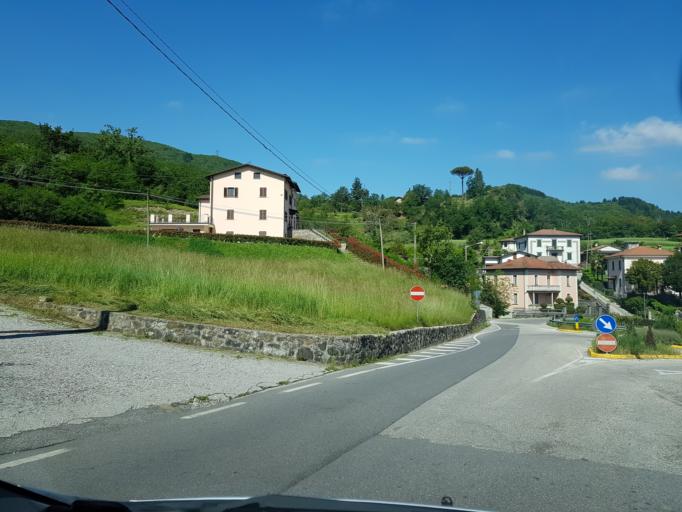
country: IT
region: Tuscany
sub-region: Provincia di Lucca
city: Camporgiano
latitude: 44.1555
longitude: 10.3366
